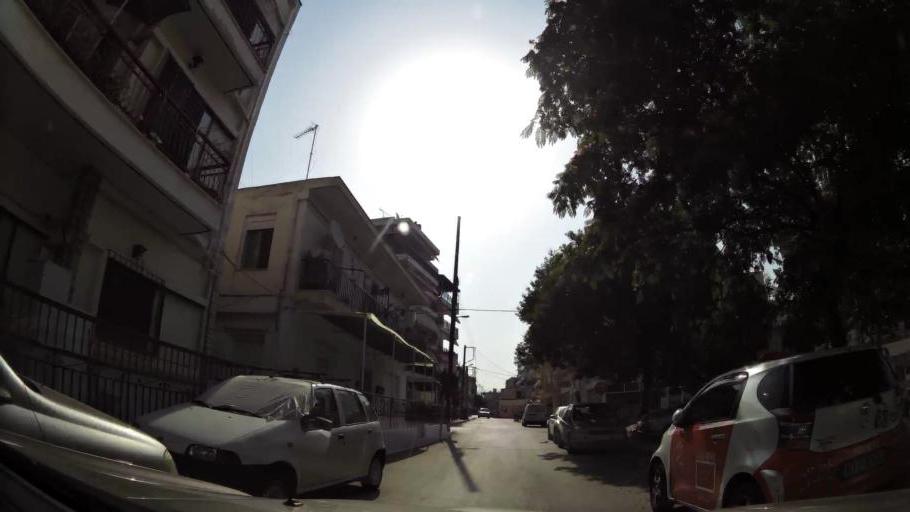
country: GR
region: Central Macedonia
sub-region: Nomos Thessalonikis
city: Ampelokipoi
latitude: 40.6650
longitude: 22.9227
